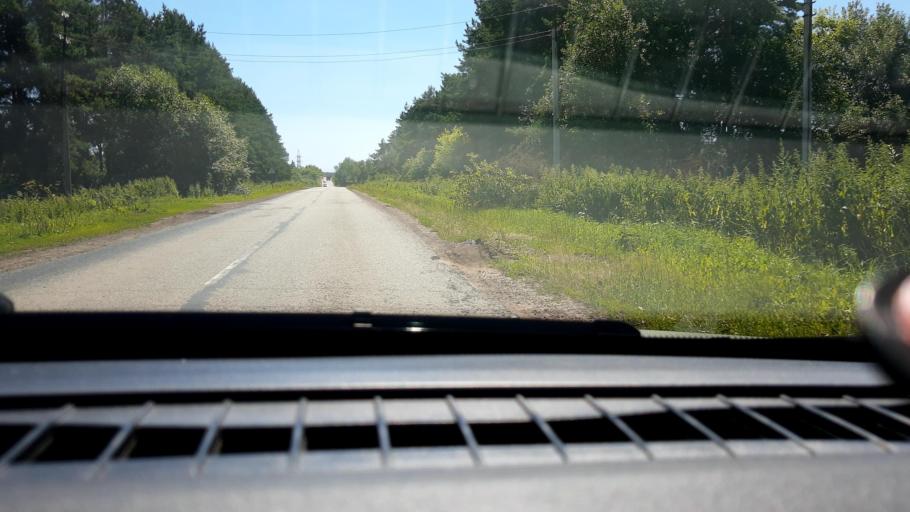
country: RU
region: Nizjnij Novgorod
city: Burevestnik
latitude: 56.1491
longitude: 43.7773
